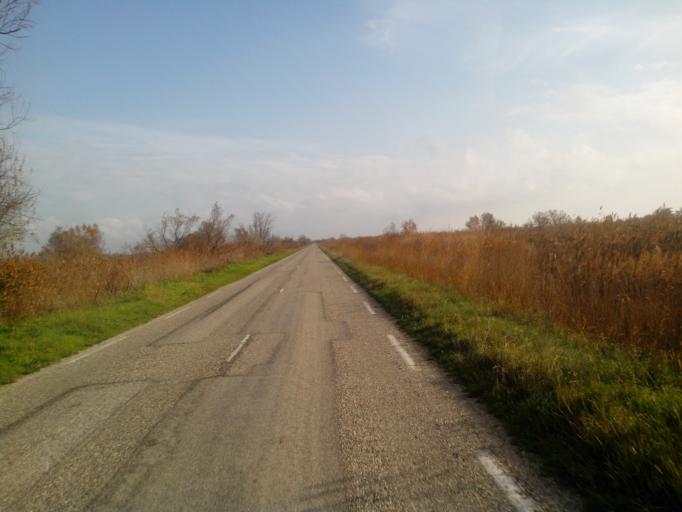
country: FR
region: Languedoc-Roussillon
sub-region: Departement du Gard
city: Saint-Gilles
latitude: 43.5785
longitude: 4.5165
